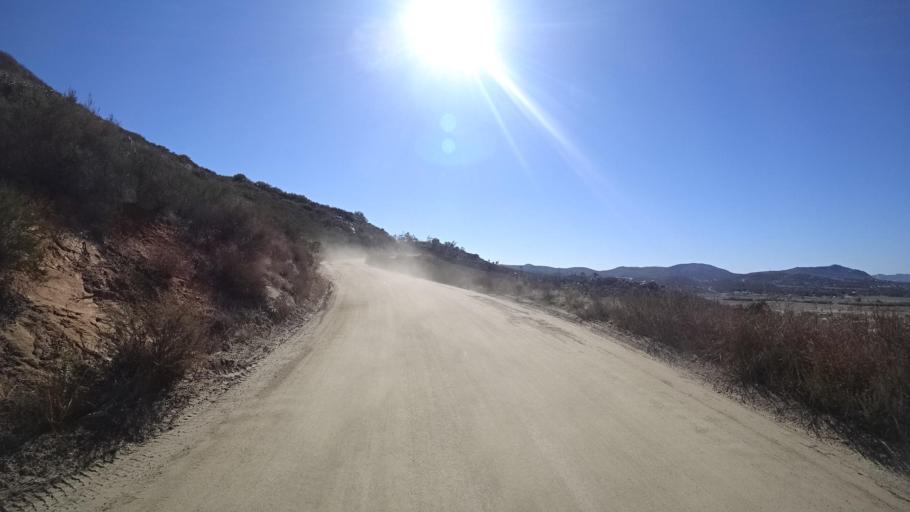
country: US
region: California
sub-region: San Diego County
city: Descanso
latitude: 32.8625
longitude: -116.6886
